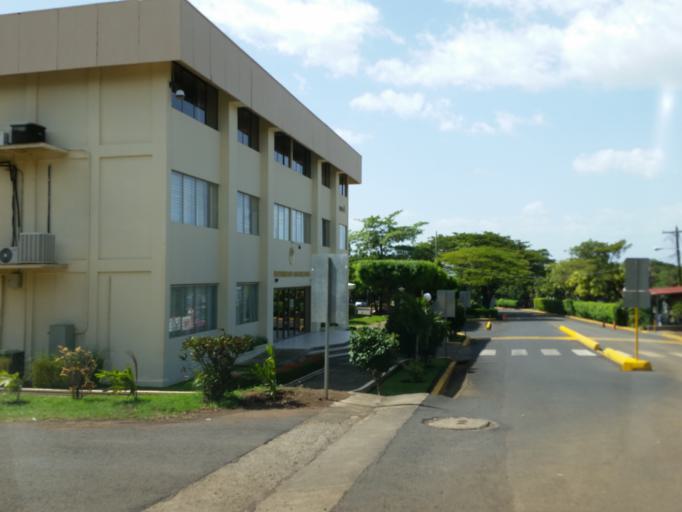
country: NI
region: Managua
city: Managua
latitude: 12.1082
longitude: -86.2565
